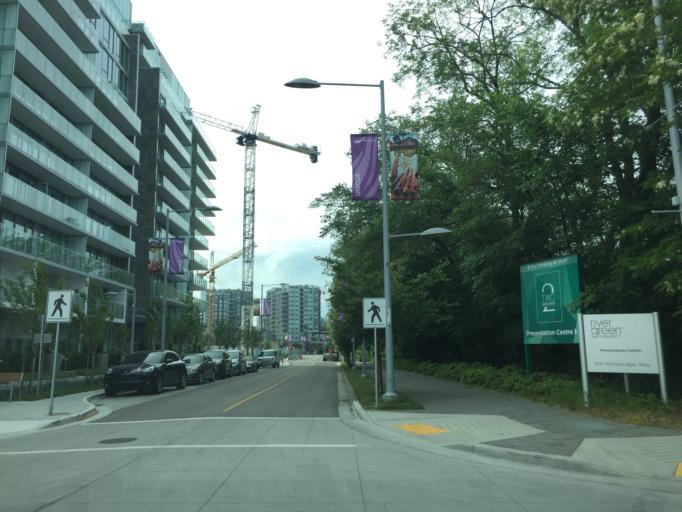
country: CA
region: British Columbia
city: Richmond
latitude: 49.1762
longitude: -123.1505
